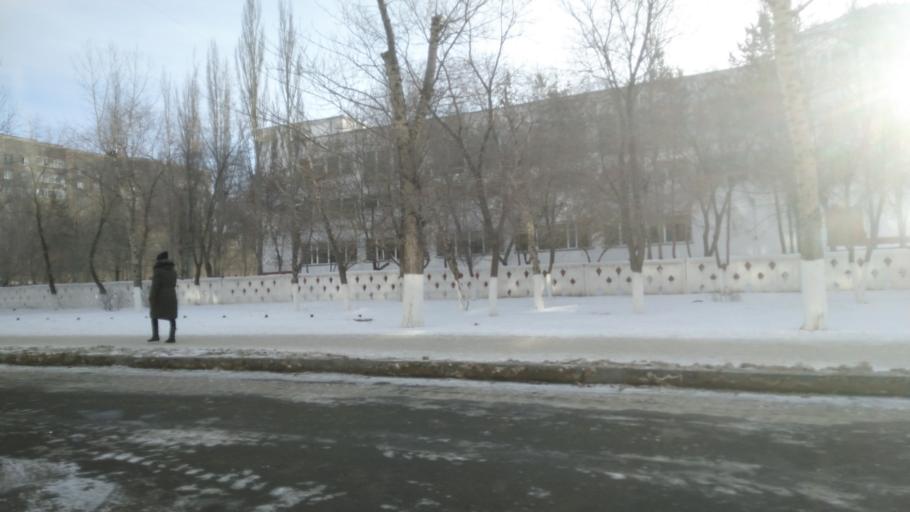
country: KZ
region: Pavlodar
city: Pavlodar
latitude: 52.2675
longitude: 76.9482
